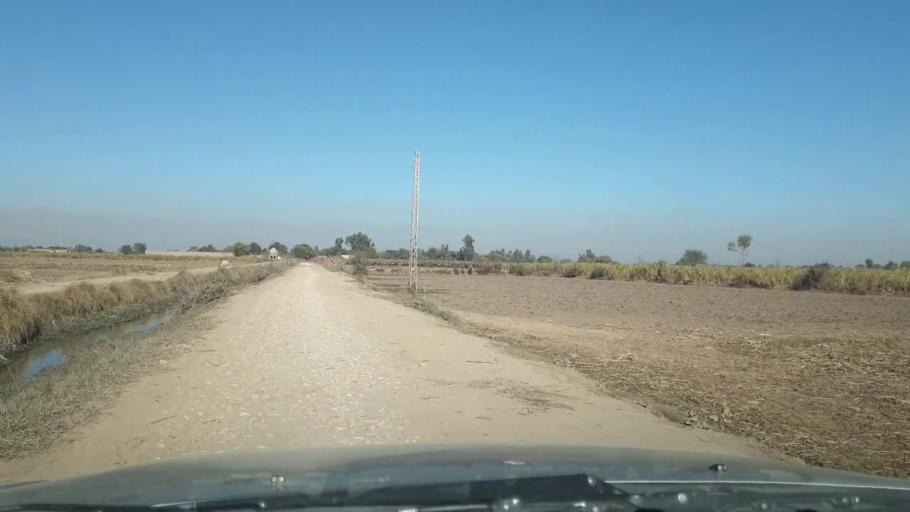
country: PK
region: Sindh
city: Ghotki
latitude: 28.0387
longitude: 69.2466
